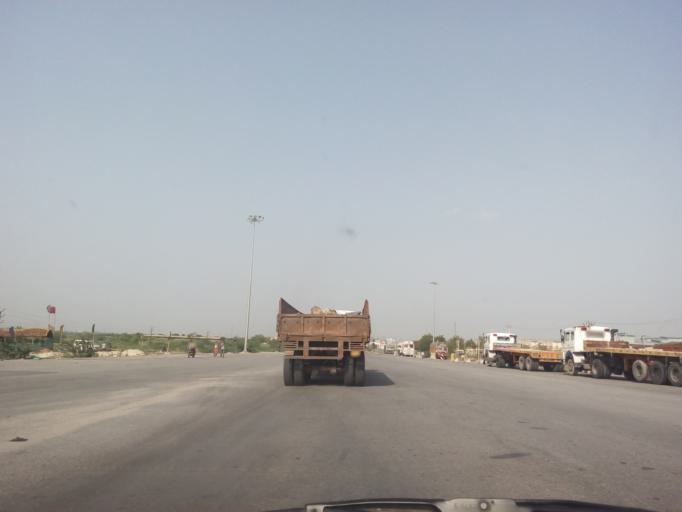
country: IN
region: Rajasthan
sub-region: Ajmer
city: Beawar
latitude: 26.1583
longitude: 74.3713
